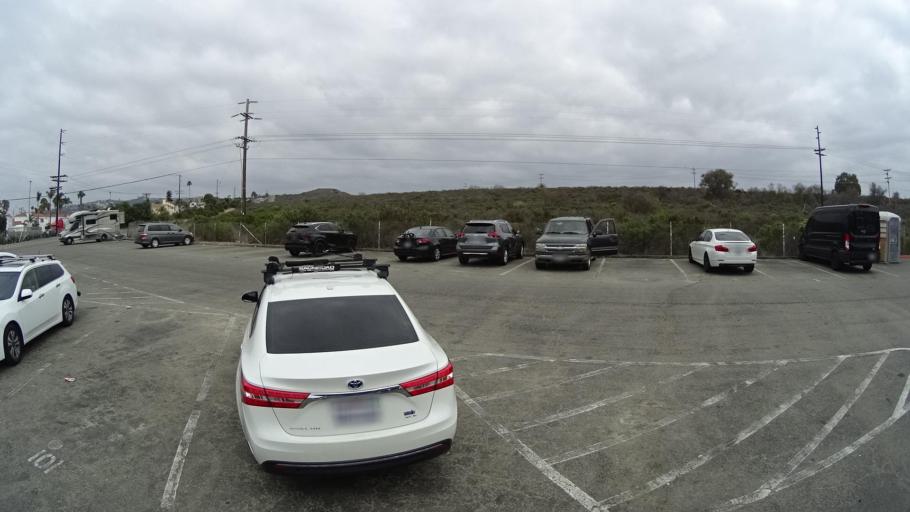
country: US
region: California
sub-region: Orange County
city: San Clemente
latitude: 33.3972
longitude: -117.5931
